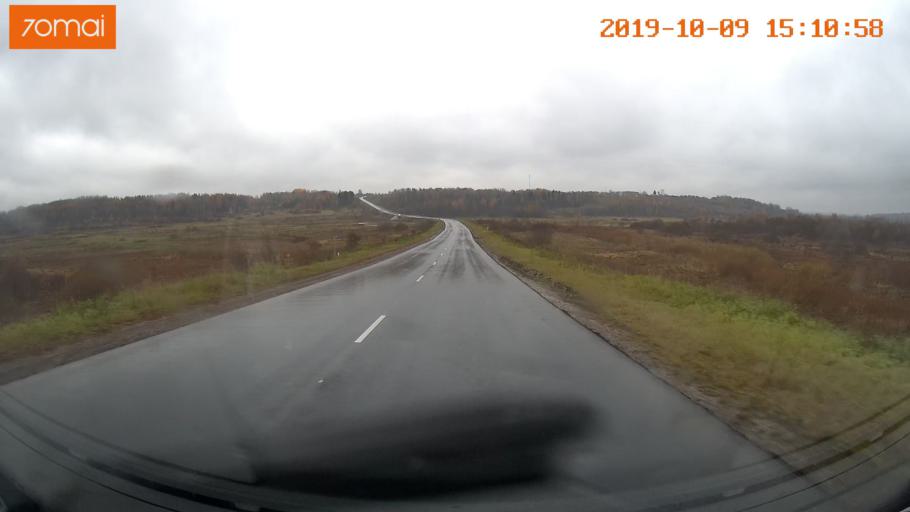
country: RU
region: Kostroma
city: Susanino
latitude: 58.1714
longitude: 41.6338
